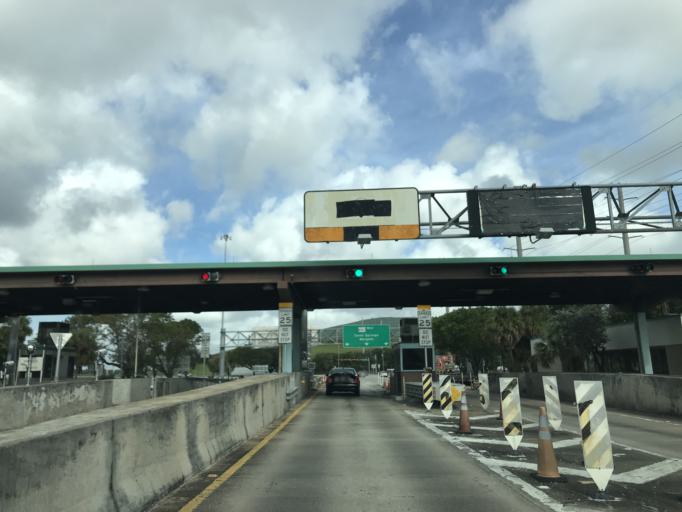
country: US
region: Florida
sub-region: Broward County
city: Coconut Creek
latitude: 26.2721
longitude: -80.1658
